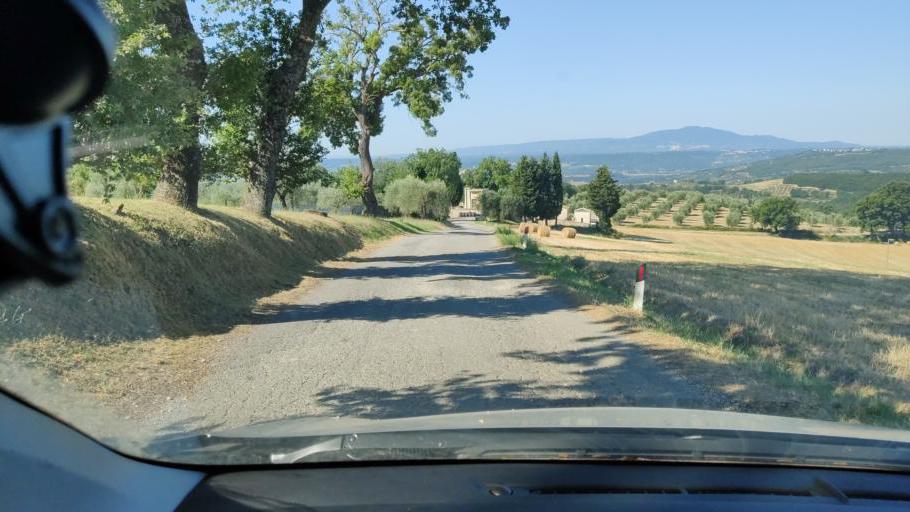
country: IT
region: Umbria
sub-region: Provincia di Terni
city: Amelia
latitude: 42.5122
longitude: 12.4235
